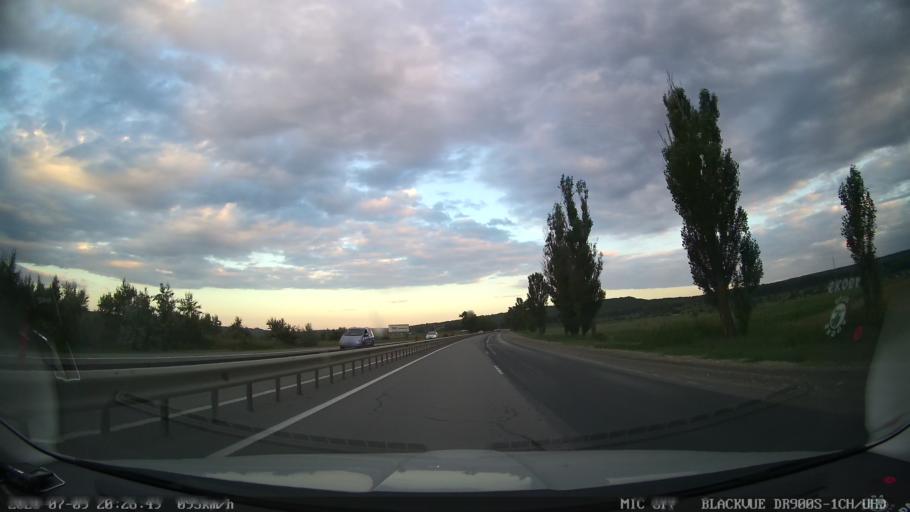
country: MD
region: Chisinau
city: Cricova
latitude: 47.1800
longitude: 28.7971
